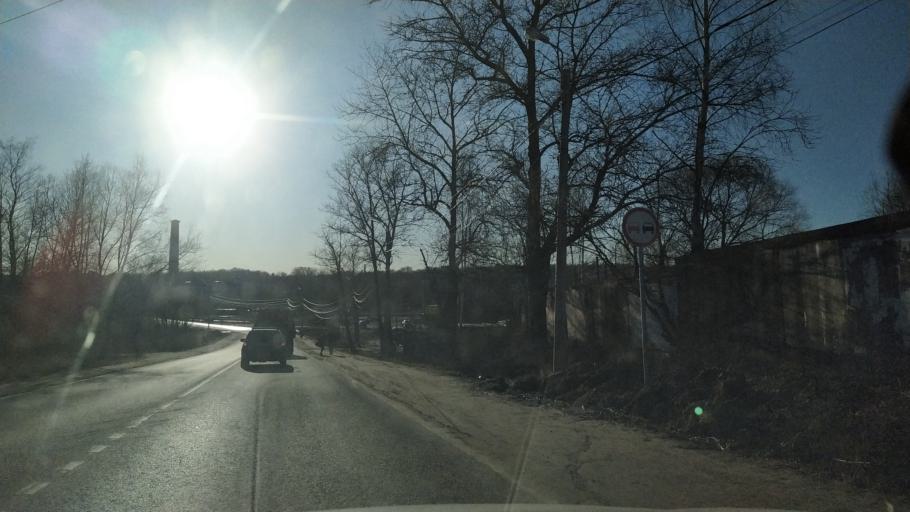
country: RU
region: St.-Petersburg
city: Krasnoye Selo
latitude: 59.7310
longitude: 30.1086
